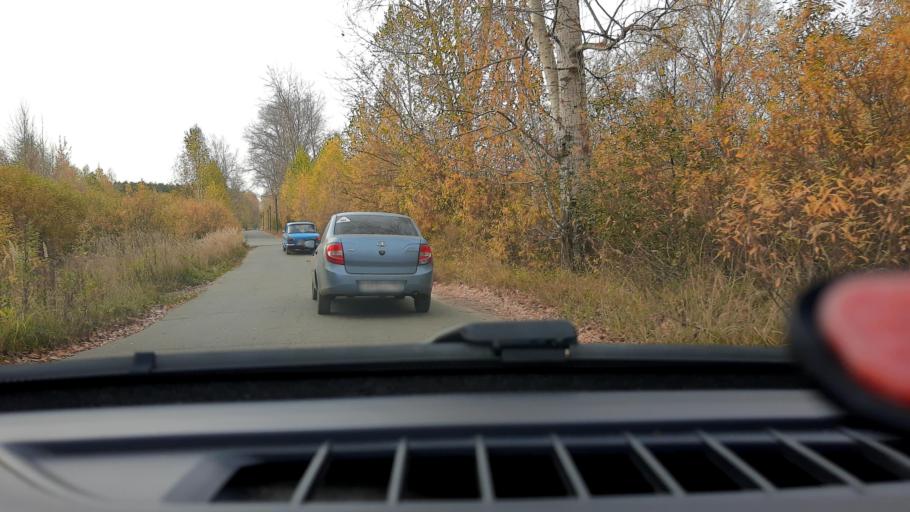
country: RU
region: Nizjnij Novgorod
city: Gorbatovka
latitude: 56.2940
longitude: 43.8329
